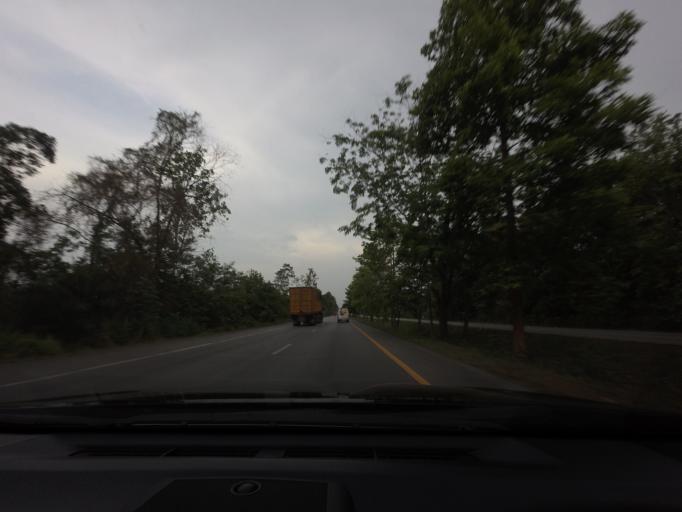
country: TH
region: Surat Thani
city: Tha Chana
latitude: 9.4796
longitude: 99.1442
